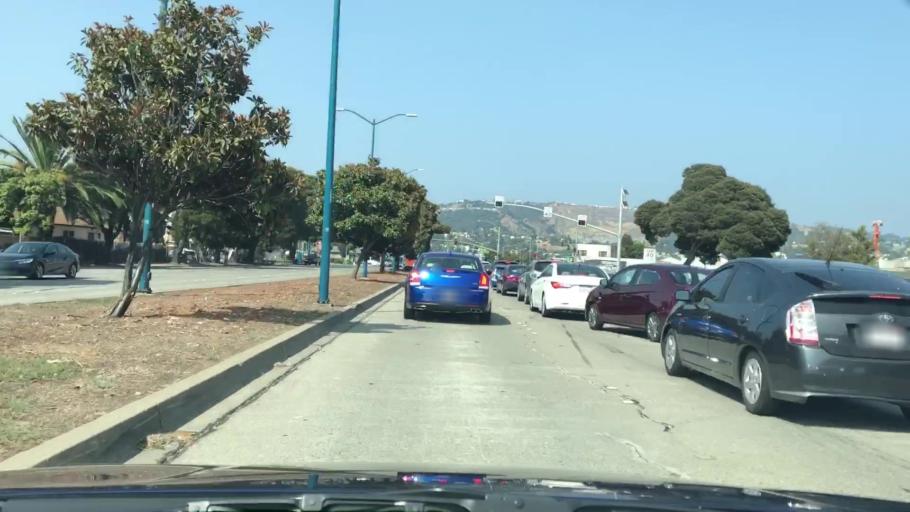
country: US
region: California
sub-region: Alameda County
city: San Leandro
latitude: 37.7578
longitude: -122.1880
